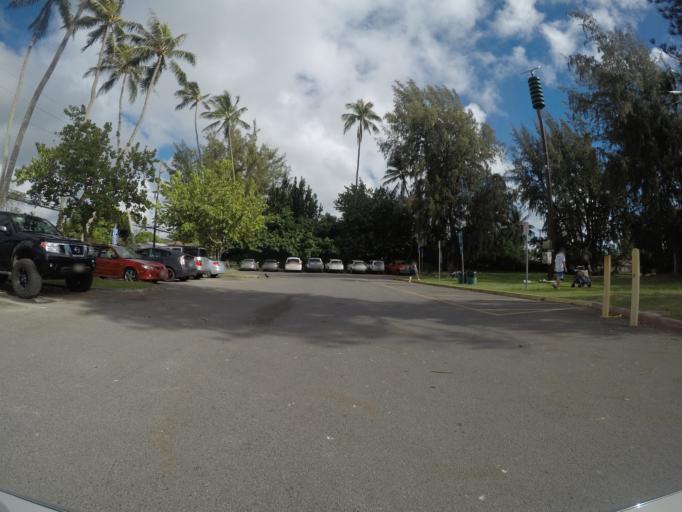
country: US
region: Hawaii
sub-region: Honolulu County
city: Kailua
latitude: 21.4041
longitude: -157.7404
